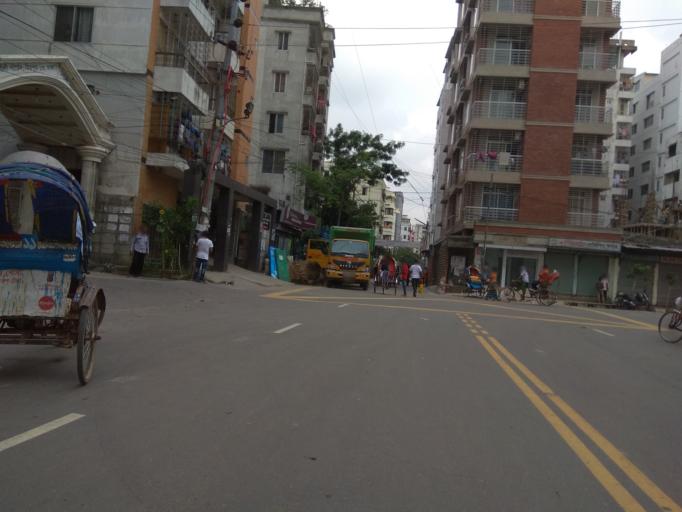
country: BD
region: Dhaka
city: Azimpur
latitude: 23.8106
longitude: 90.3770
